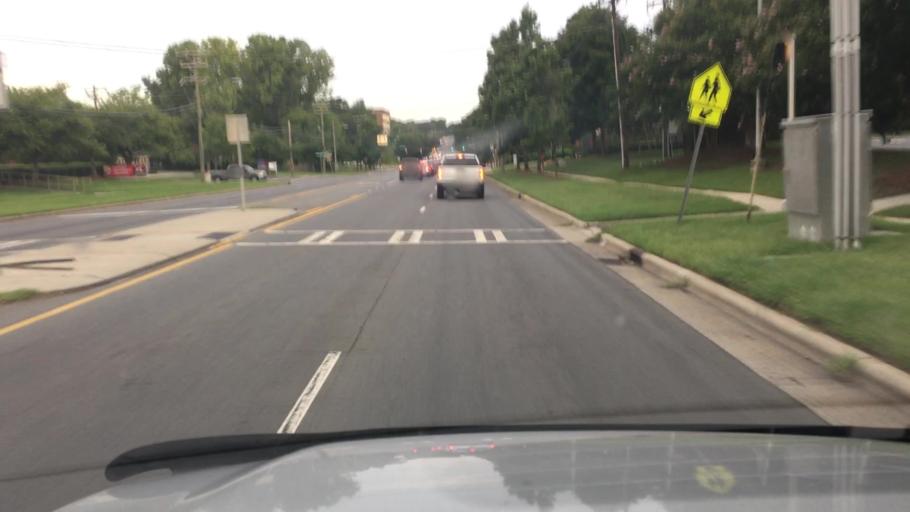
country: US
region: North Carolina
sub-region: Mecklenburg County
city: Pineville
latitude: 35.0878
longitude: -80.8498
